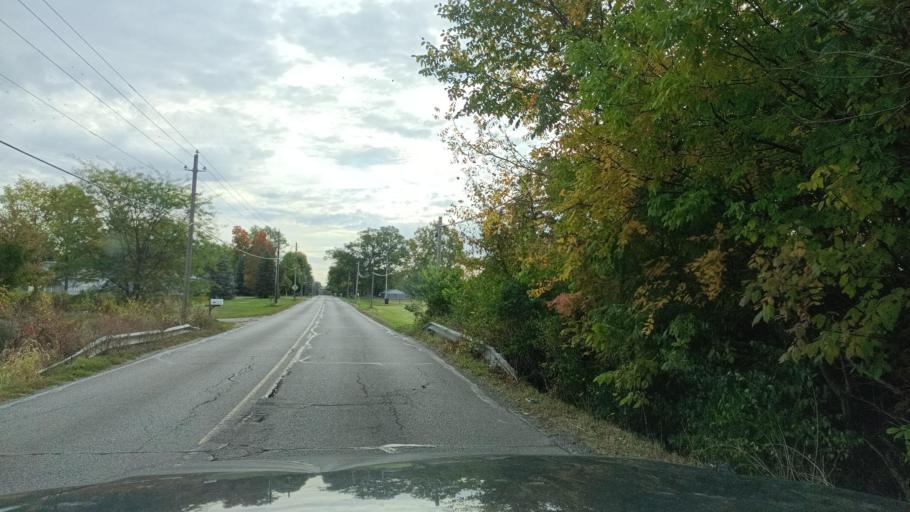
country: US
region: Indiana
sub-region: Delaware County
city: Yorktown
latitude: 40.2044
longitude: -85.4583
